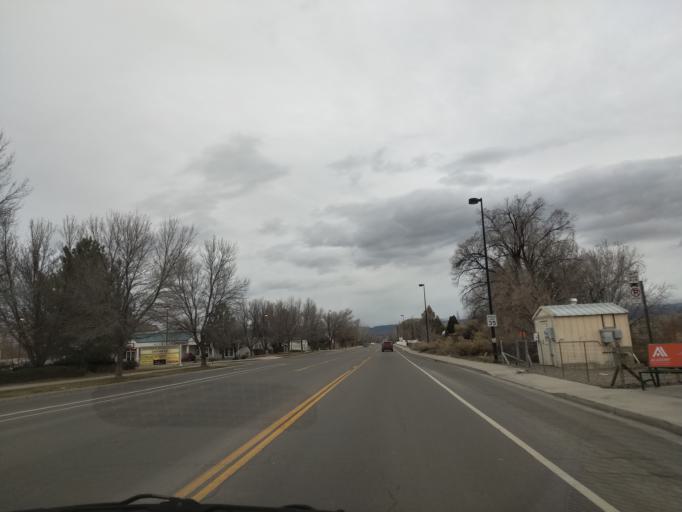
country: US
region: Colorado
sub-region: Mesa County
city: Fruitvale
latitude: 39.0913
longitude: -108.5152
